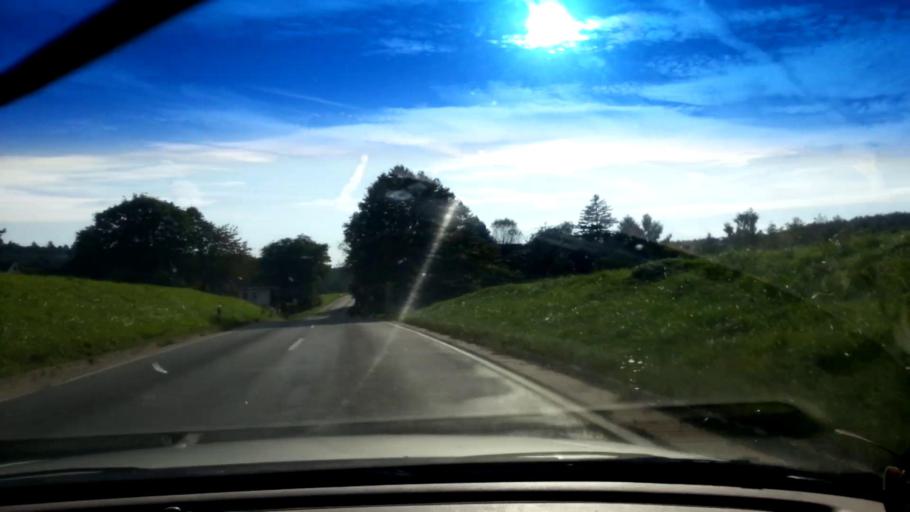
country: DE
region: Bavaria
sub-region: Upper Franconia
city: Baunach
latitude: 49.9779
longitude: 10.8237
